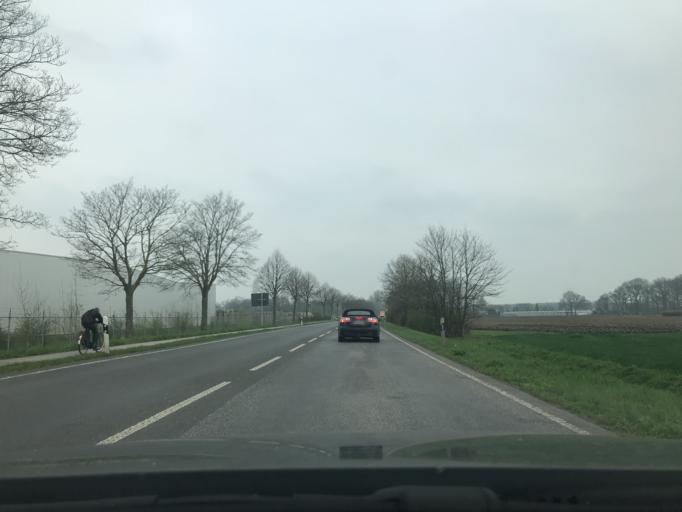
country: DE
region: North Rhine-Westphalia
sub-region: Regierungsbezirk Dusseldorf
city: Kevelaer
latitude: 51.5628
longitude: 6.2645
